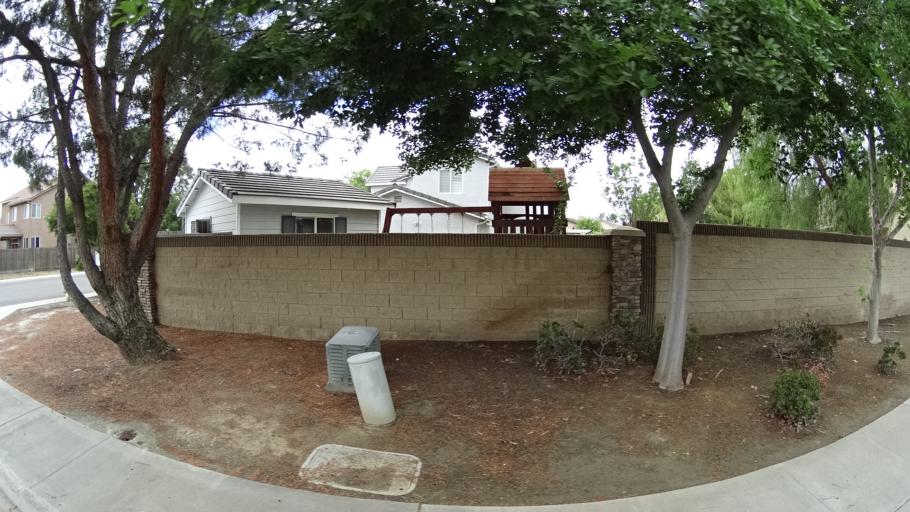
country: US
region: California
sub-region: Kings County
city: Armona
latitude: 36.3338
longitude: -119.6795
